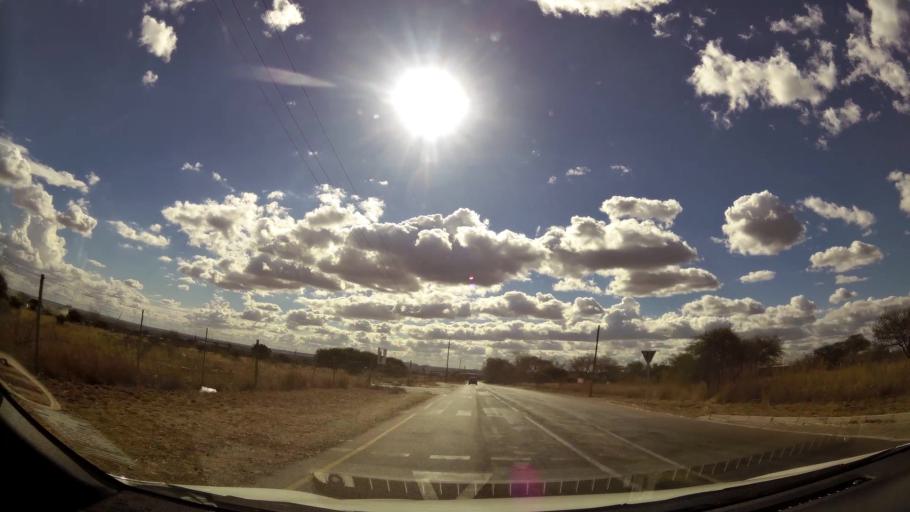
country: ZA
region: Limpopo
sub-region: Capricorn District Municipality
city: Polokwane
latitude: -23.8772
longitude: 29.4803
